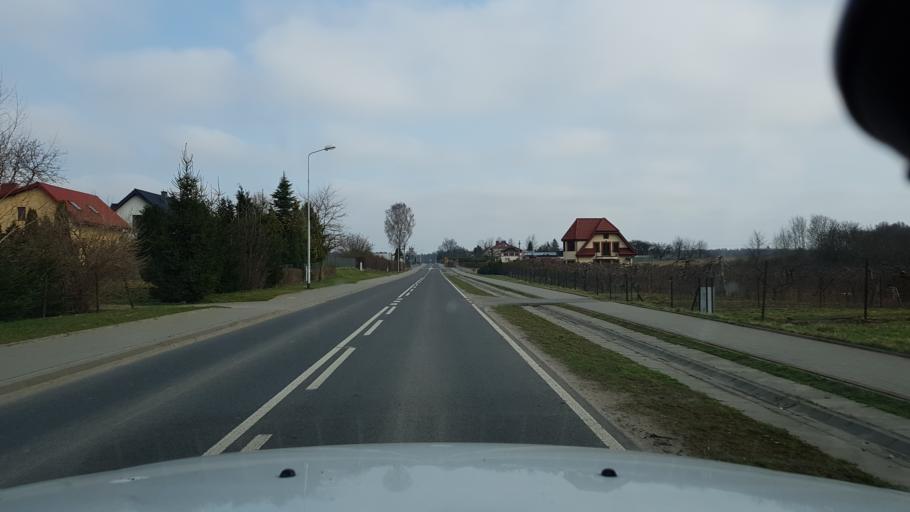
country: PL
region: West Pomeranian Voivodeship
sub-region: Powiat koszalinski
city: Sianow
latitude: 54.2619
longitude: 16.2667
